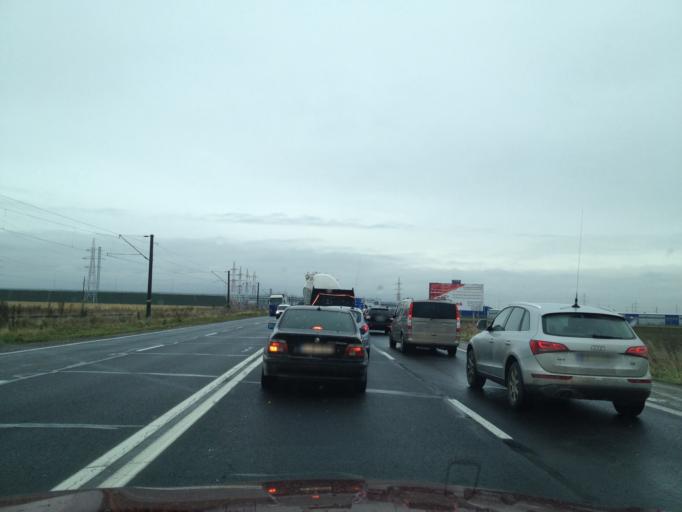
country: RO
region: Brasov
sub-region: Comuna Harman
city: Harman
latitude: 45.6882
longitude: 25.6693
